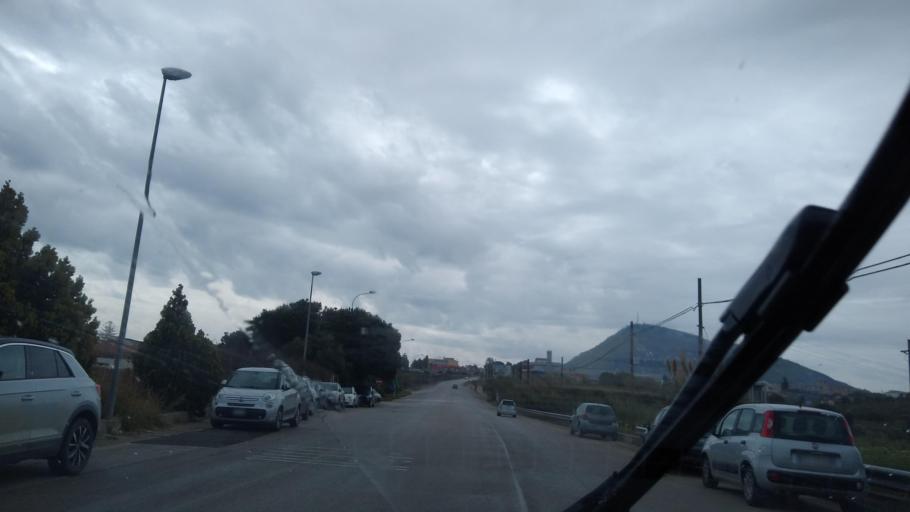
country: IT
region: Sicily
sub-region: Trapani
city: Alcamo
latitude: 38.0009
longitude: 12.9561
